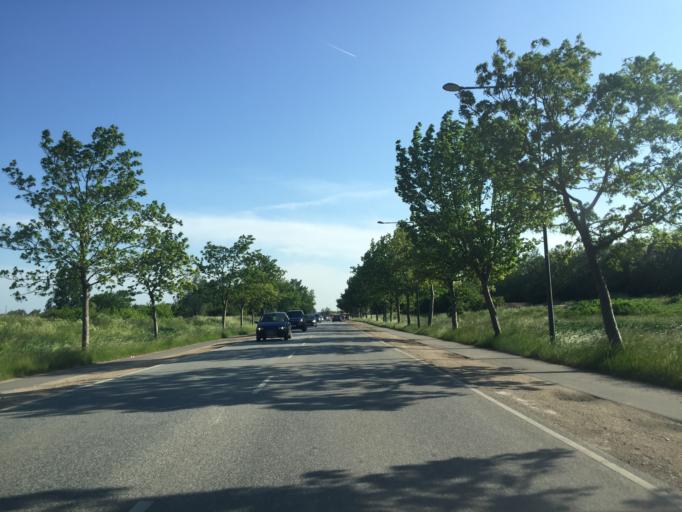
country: DK
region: Capital Region
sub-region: Kobenhavn
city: Copenhagen
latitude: 55.6443
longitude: 12.5652
